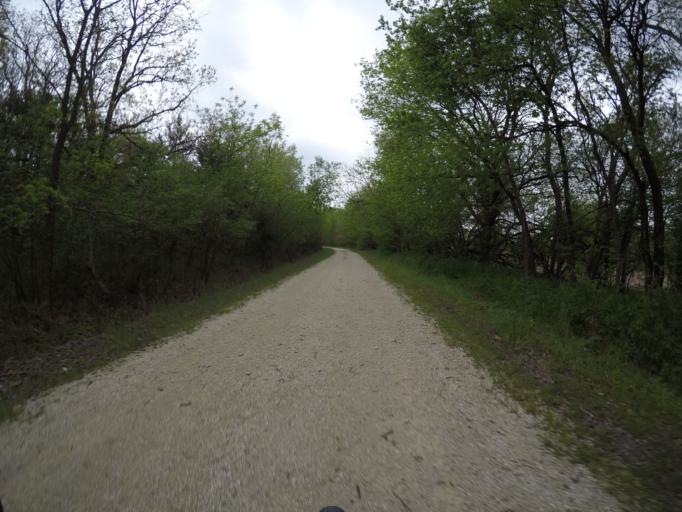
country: US
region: Nebraska
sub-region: Gage County
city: Wymore
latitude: 40.1285
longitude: -96.6443
